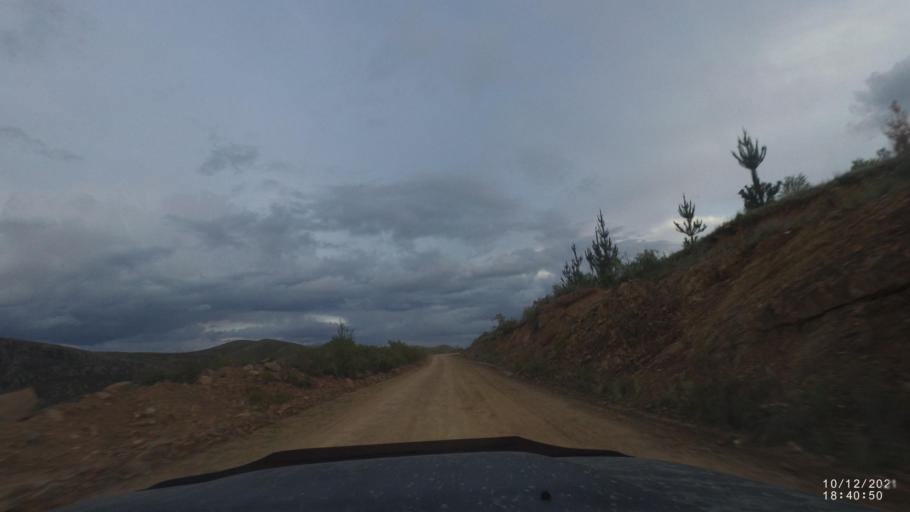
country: BO
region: Cochabamba
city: Tarata
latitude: -17.8596
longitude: -65.9893
